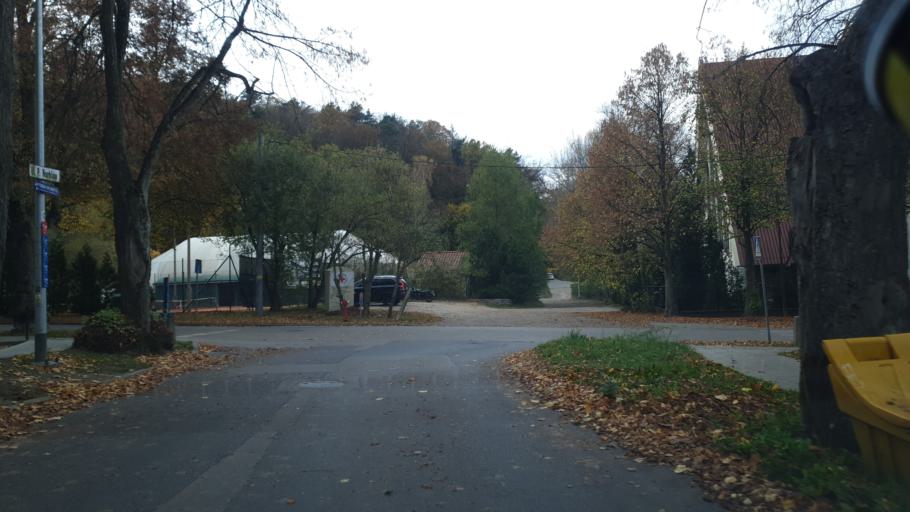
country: PL
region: Pomeranian Voivodeship
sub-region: Sopot
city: Sopot
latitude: 54.3894
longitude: 18.5685
